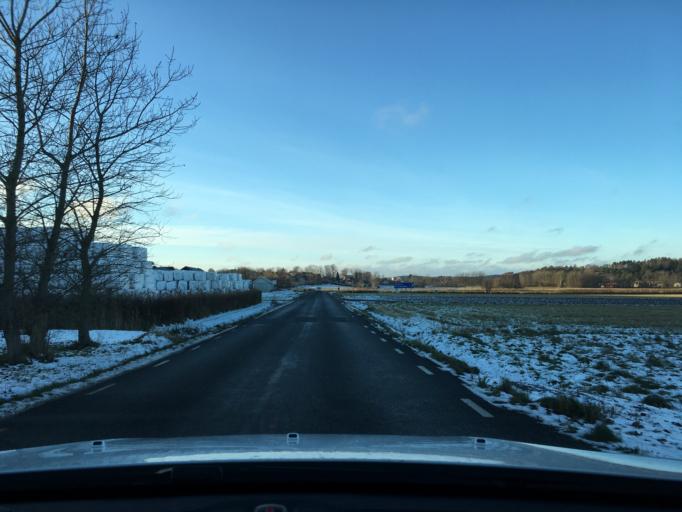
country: SE
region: Vaestra Goetaland
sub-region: Tjorns Kommun
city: Myggenas
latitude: 58.0465
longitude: 11.7257
